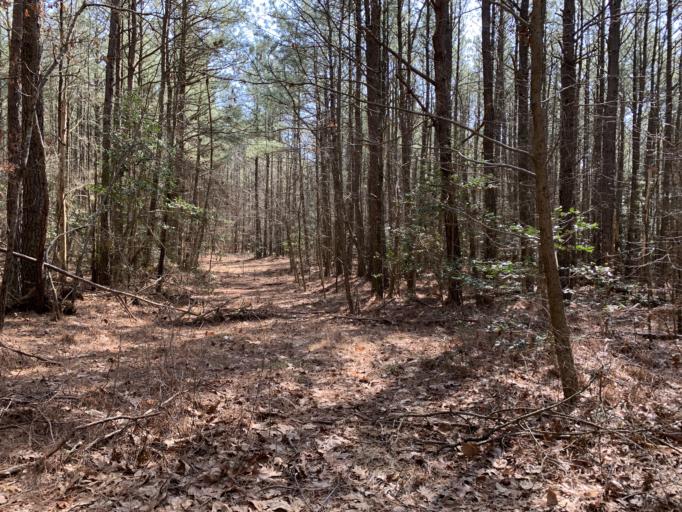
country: US
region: Delaware
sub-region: Sussex County
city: Georgetown
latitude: 38.6787
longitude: -75.4744
